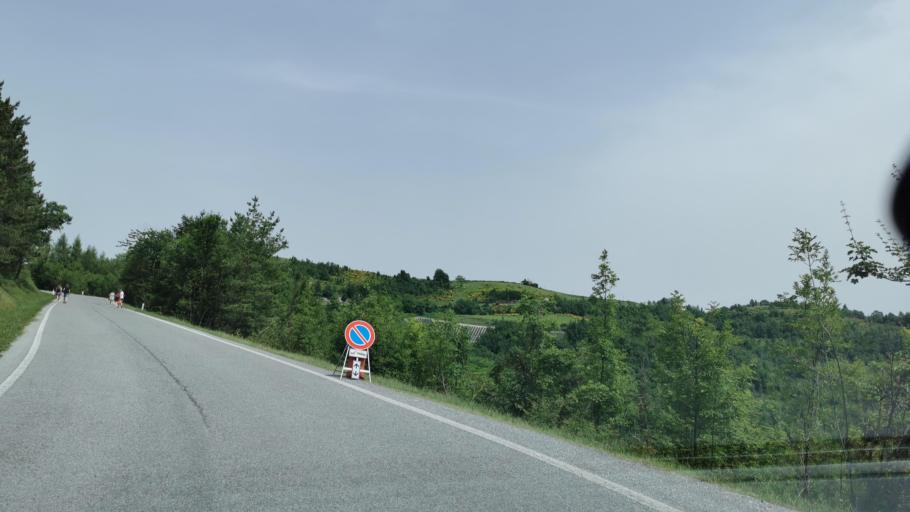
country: IT
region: Piedmont
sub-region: Provincia di Cuneo
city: Sale San Giovanni
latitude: 44.4064
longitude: 8.0777
